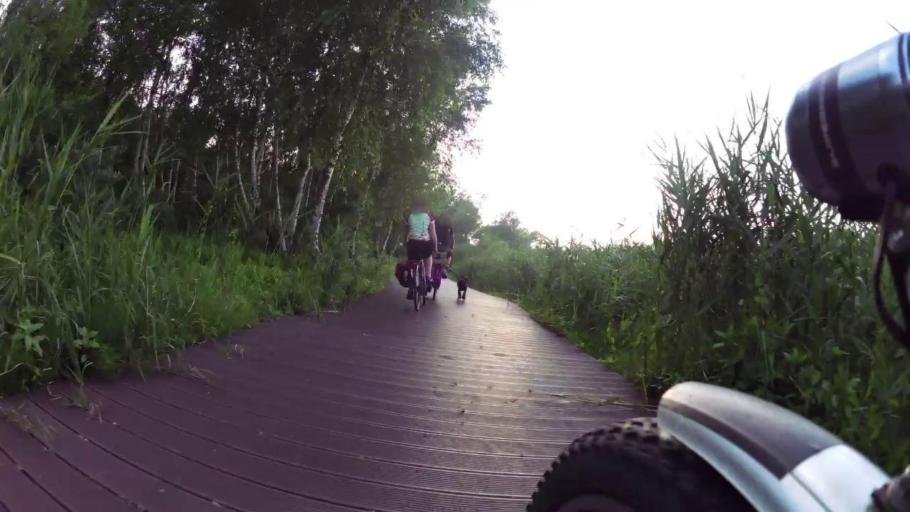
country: PL
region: West Pomeranian Voivodeship
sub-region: Powiat goleniowski
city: Stepnica
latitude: 53.6676
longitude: 14.5004
